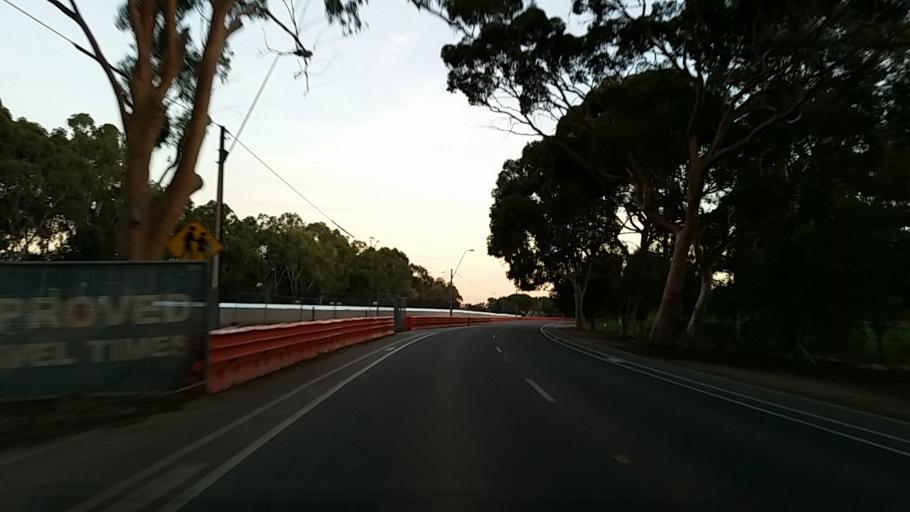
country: AU
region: South Australia
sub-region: Adelaide
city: North Adelaide
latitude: -34.9127
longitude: 138.5830
